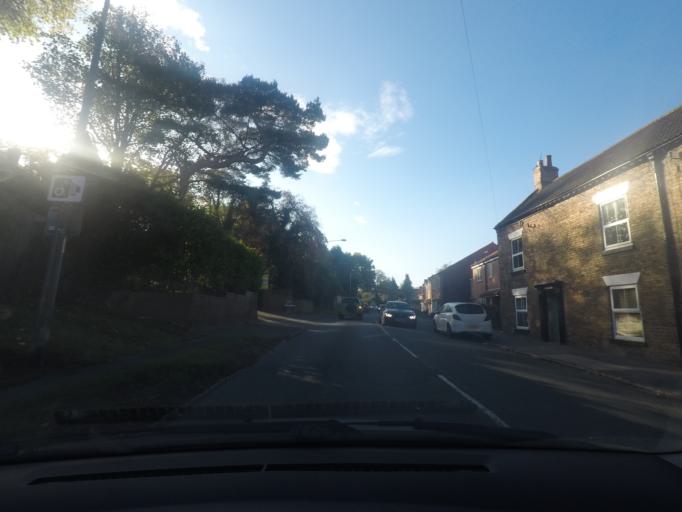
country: GB
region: England
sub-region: East Riding of Yorkshire
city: South Cave
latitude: 53.7679
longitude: -0.6002
